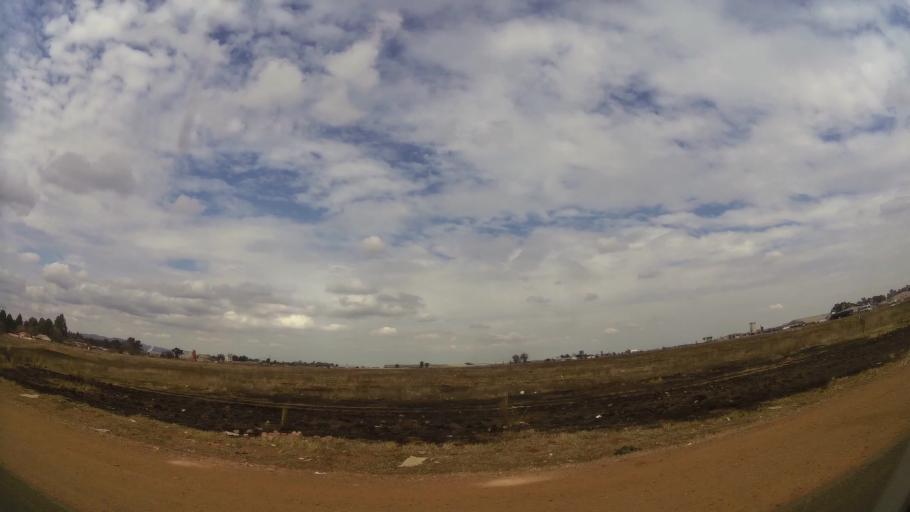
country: ZA
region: Gauteng
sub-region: Sedibeng District Municipality
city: Meyerton
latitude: -26.4173
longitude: 28.0805
